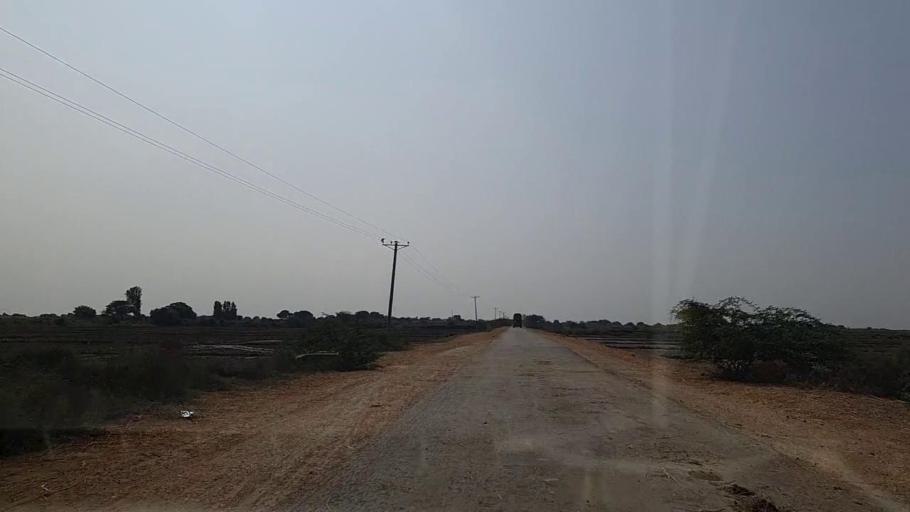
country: PK
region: Sindh
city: Chuhar Jamali
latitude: 24.2812
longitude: 67.9198
